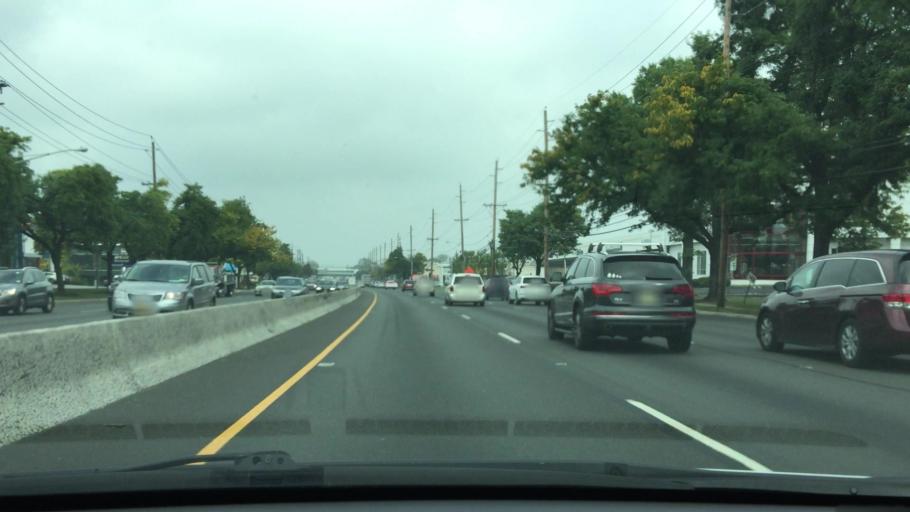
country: US
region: New Jersey
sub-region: Bergen County
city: Paramus
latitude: 40.9300
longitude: -74.0705
